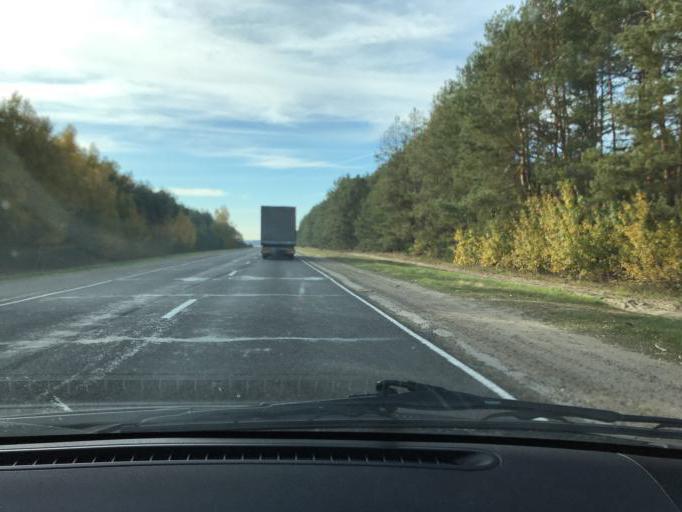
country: BY
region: Brest
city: Horad Pinsk
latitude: 52.1519
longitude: 25.8366
